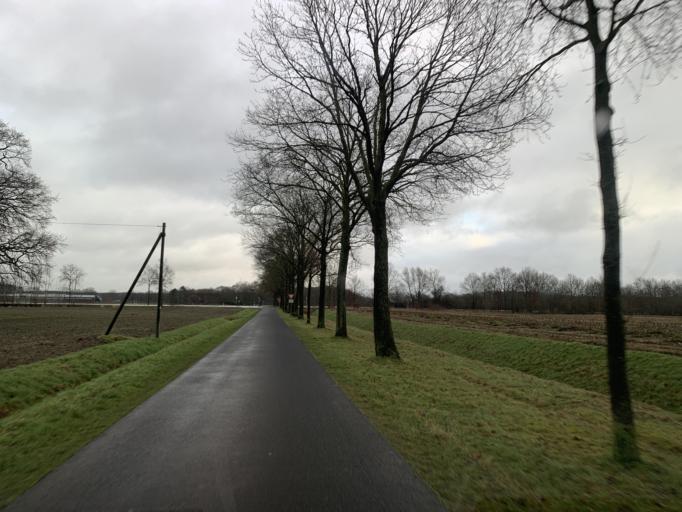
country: DE
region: North Rhine-Westphalia
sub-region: Regierungsbezirk Munster
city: Senden
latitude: 51.9053
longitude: 7.5273
